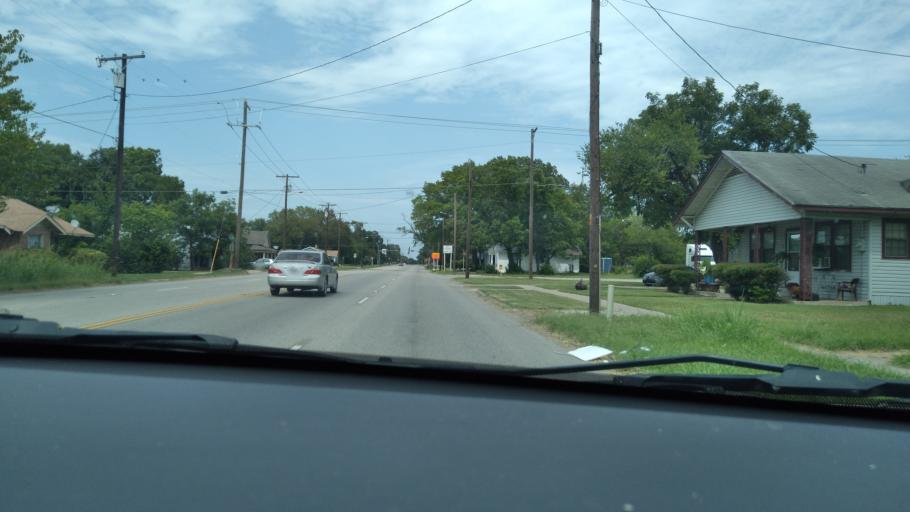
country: US
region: Texas
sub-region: Navarro County
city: Corsicana
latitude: 32.0947
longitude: -96.4570
